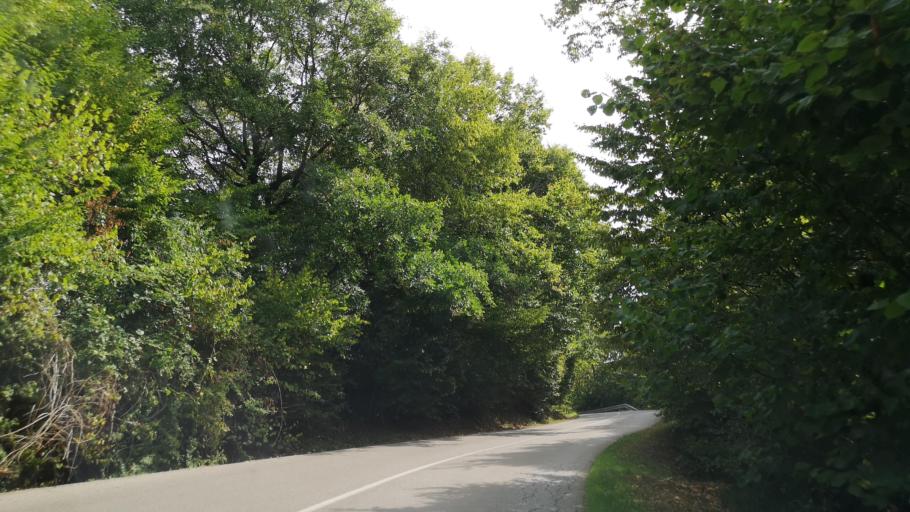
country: SK
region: Banskobystricky
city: Revuca
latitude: 48.6037
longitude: 20.1557
